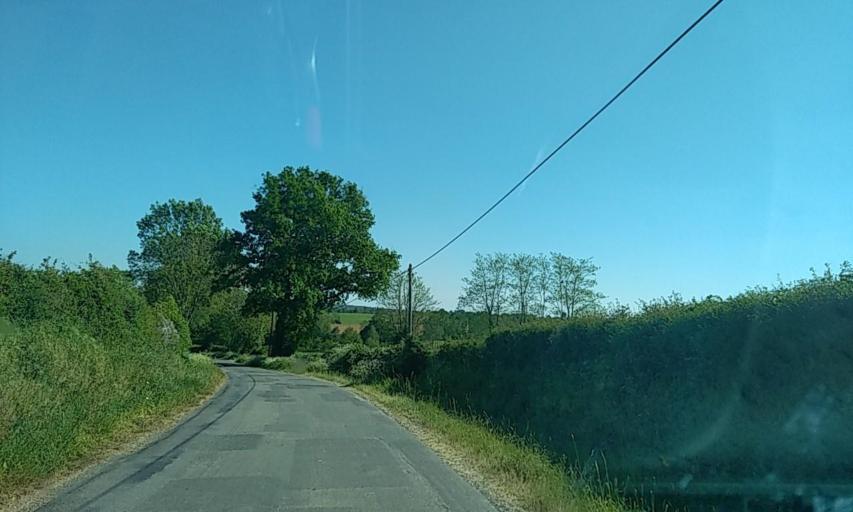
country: FR
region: Poitou-Charentes
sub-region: Departement des Deux-Sevres
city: Boisme
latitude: 46.7757
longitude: -0.4146
